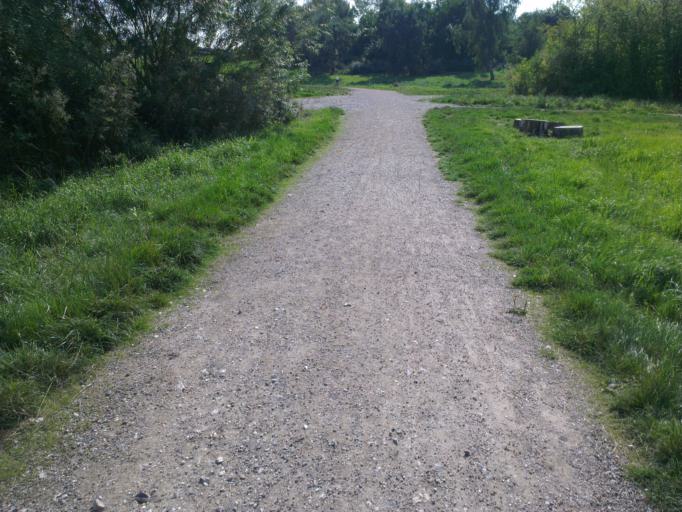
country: DK
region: Capital Region
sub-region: Frederikssund Kommune
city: Frederikssund
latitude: 55.8335
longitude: 12.0843
